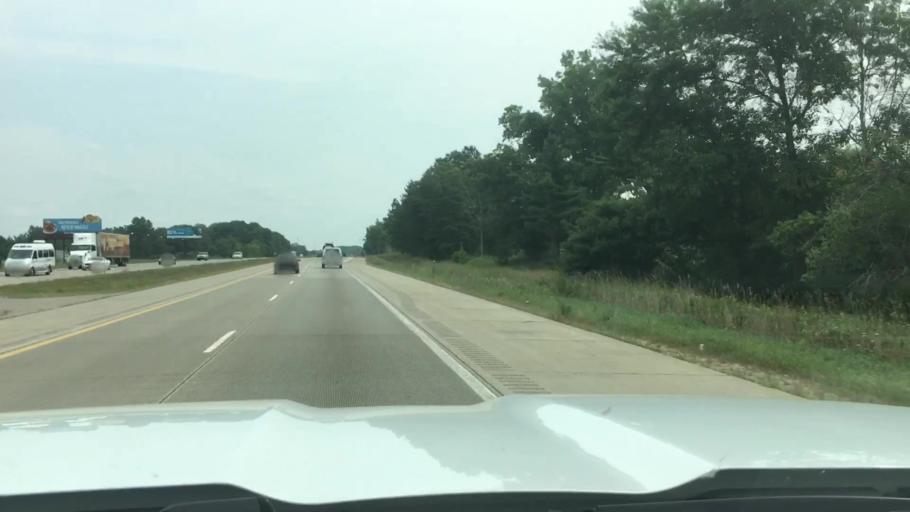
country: US
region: Michigan
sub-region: Ingham County
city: Okemos
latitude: 42.6779
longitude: -84.4506
